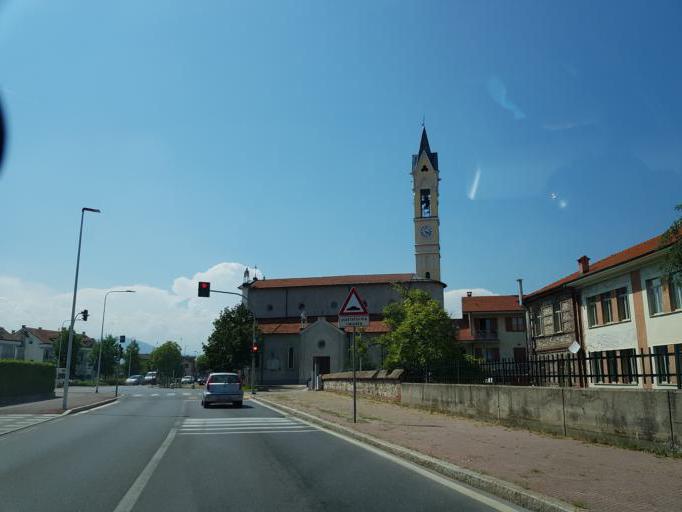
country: IT
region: Piedmont
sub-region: Provincia di Cuneo
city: Cuneo
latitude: 44.3943
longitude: 7.5196
